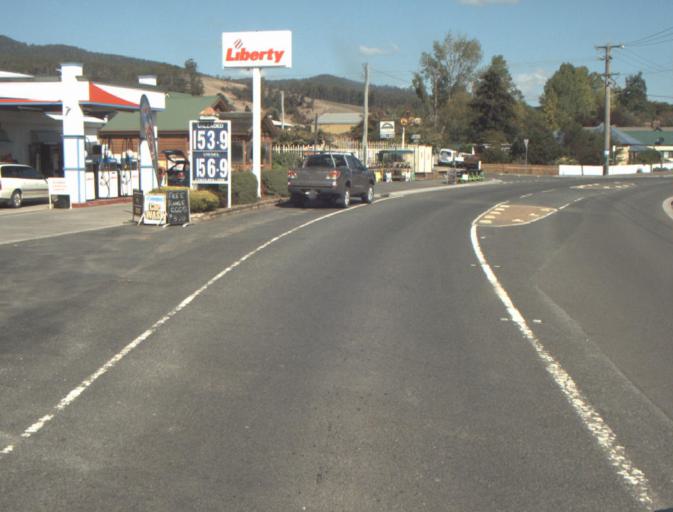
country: AU
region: Tasmania
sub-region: Launceston
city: Mayfield
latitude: -41.2485
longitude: 147.2178
